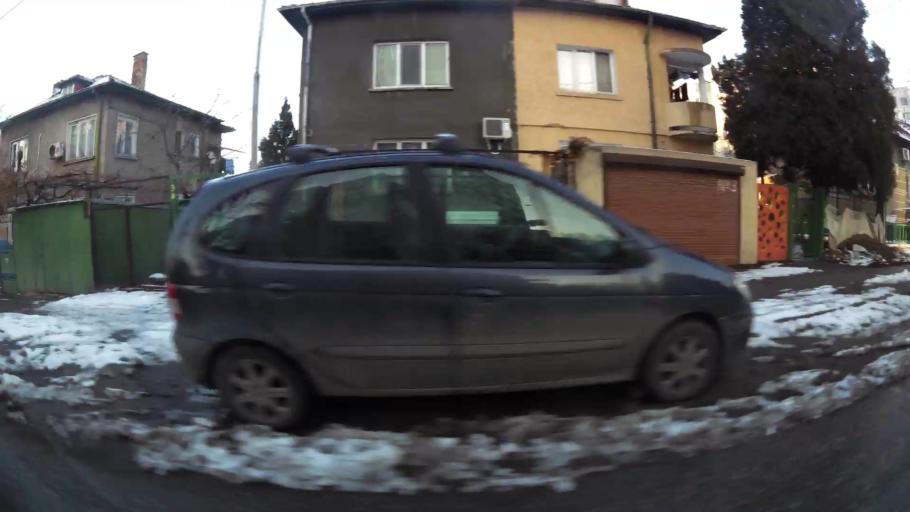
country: BG
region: Sofia-Capital
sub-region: Stolichna Obshtina
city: Sofia
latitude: 42.6938
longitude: 23.3608
